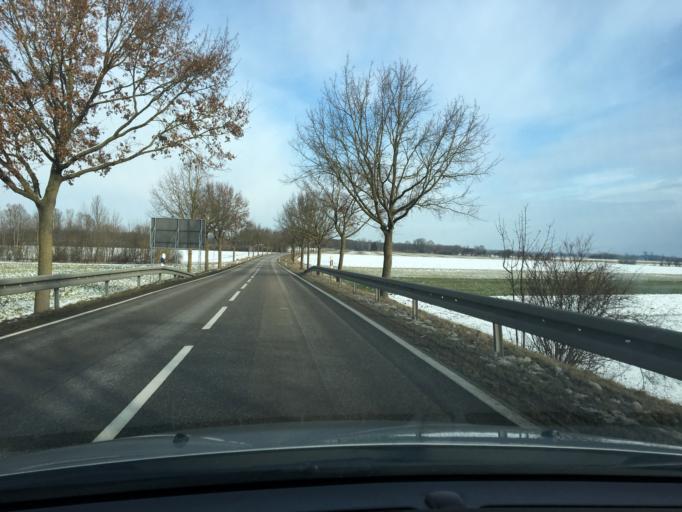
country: DE
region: Bavaria
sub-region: Upper Bavaria
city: Oberding
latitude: 48.3607
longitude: 11.8341
